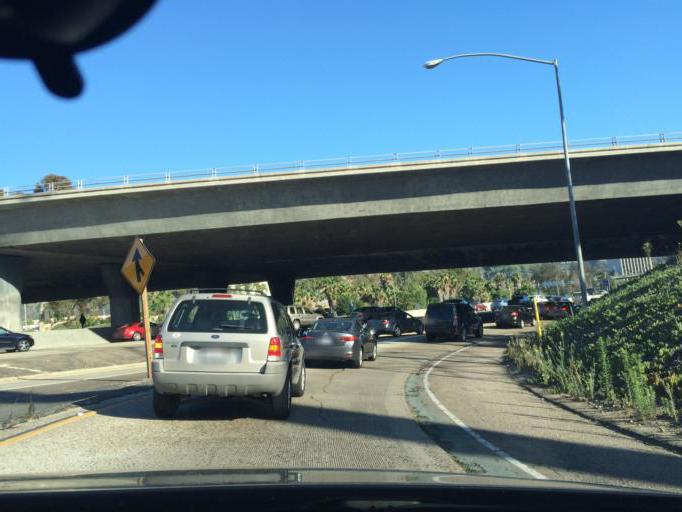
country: US
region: California
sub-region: San Diego County
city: San Diego
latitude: 32.7720
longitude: -117.1617
